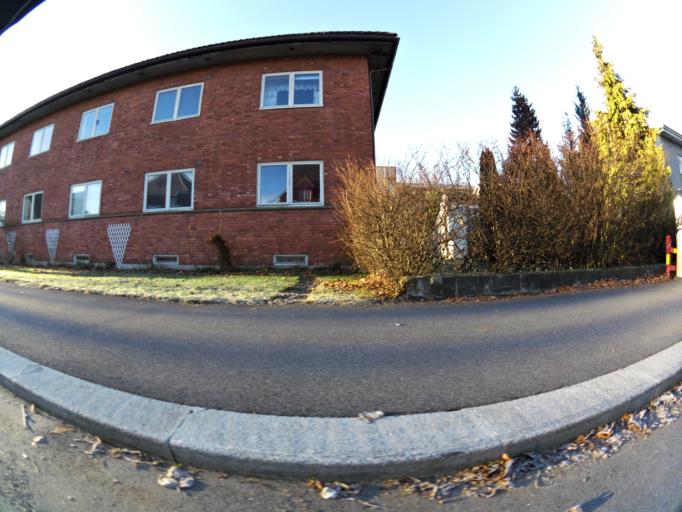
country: NO
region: Ostfold
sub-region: Fredrikstad
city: Fredrikstad
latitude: 59.2057
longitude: 10.9454
